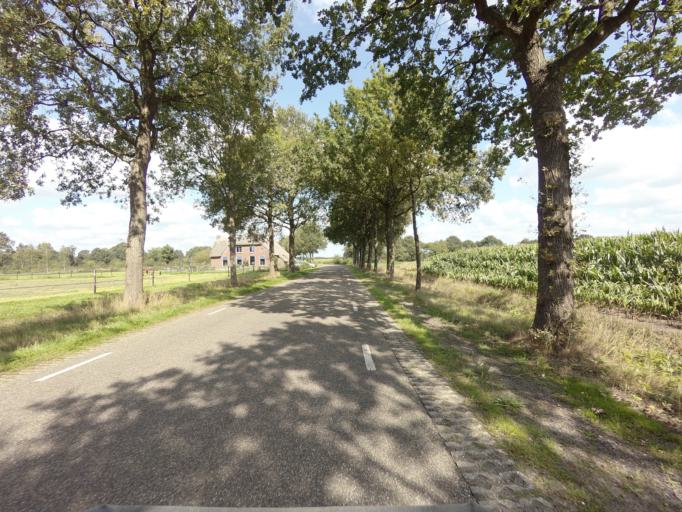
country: NL
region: Drenthe
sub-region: Gemeente Westerveld
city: Dwingeloo
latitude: 52.8574
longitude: 6.3894
